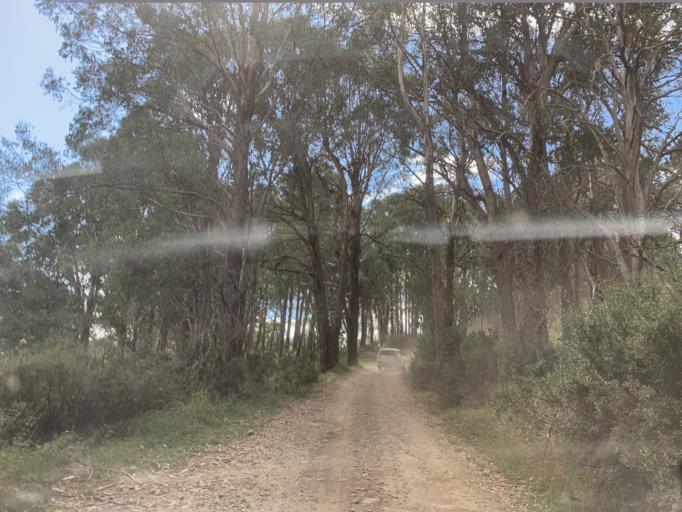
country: AU
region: Victoria
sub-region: Mansfield
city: Mansfield
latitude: -37.1056
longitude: 146.5358
